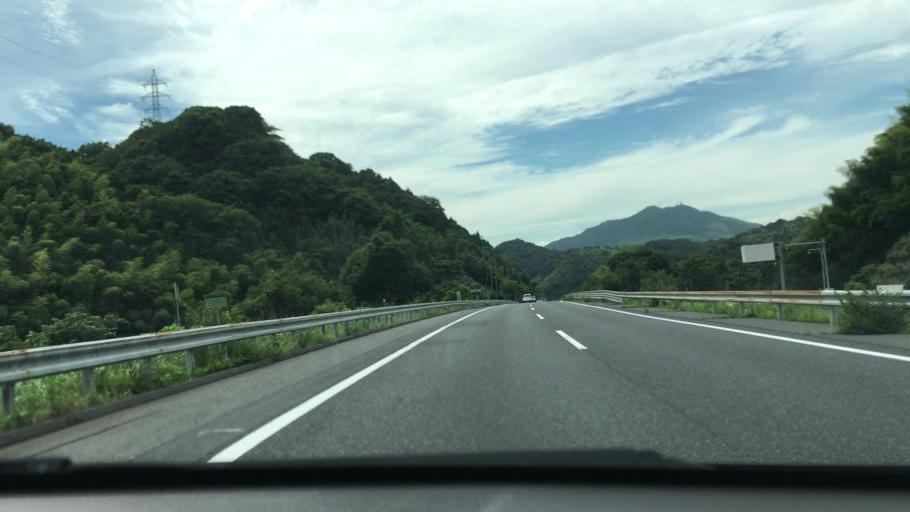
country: JP
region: Yamaguchi
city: Tokuyama
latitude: 34.0741
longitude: 131.8059
